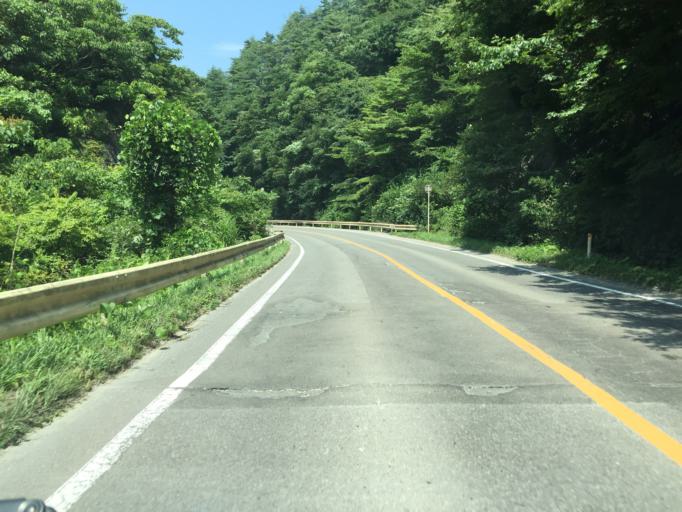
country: JP
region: Miyagi
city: Marumori
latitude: 37.8539
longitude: 140.8521
